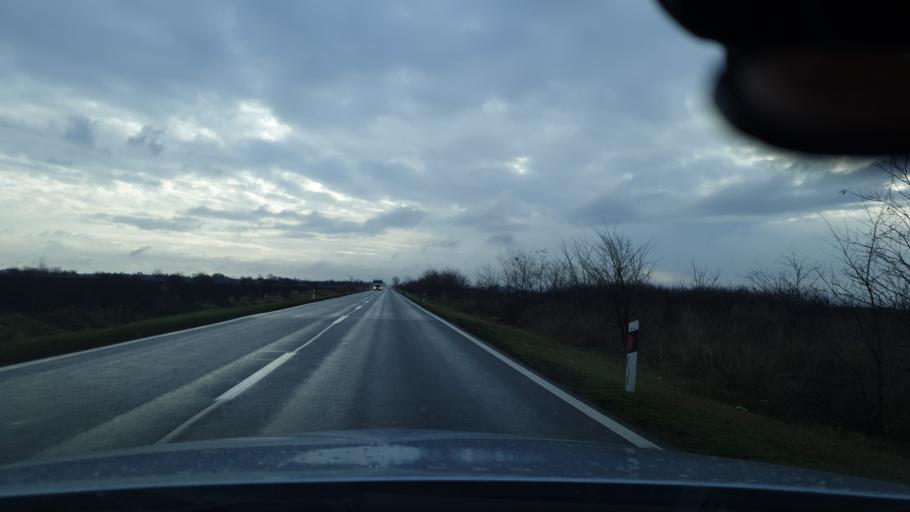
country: RS
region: Autonomna Pokrajina Vojvodina
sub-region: Juznobanatski Okrug
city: Kovin
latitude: 44.7757
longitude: 20.9376
